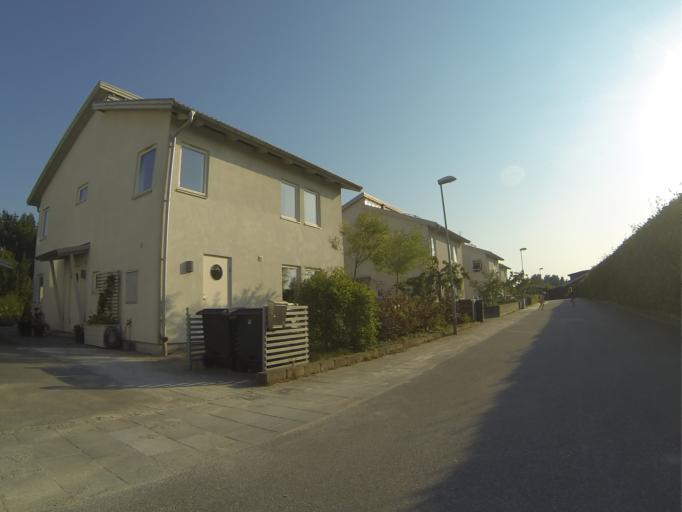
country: SE
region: Skane
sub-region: Lunds Kommun
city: Genarp
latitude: 55.7222
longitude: 13.3616
